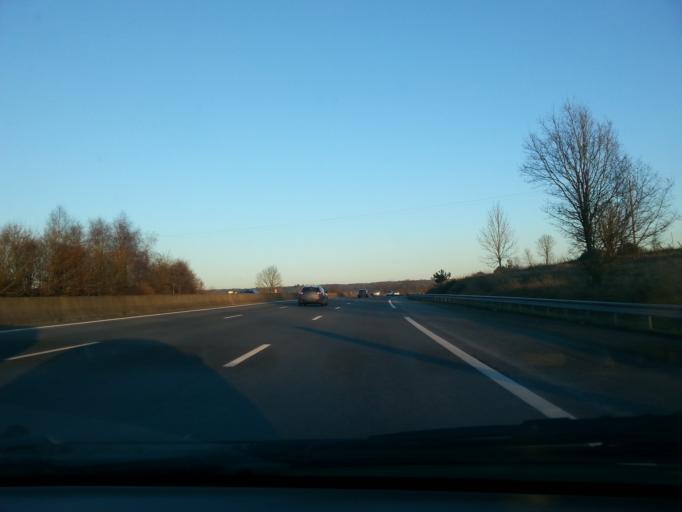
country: FR
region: Centre
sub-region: Departement d'Eure-et-Loir
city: Authon-du-Perche
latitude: 48.1920
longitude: 0.8169
